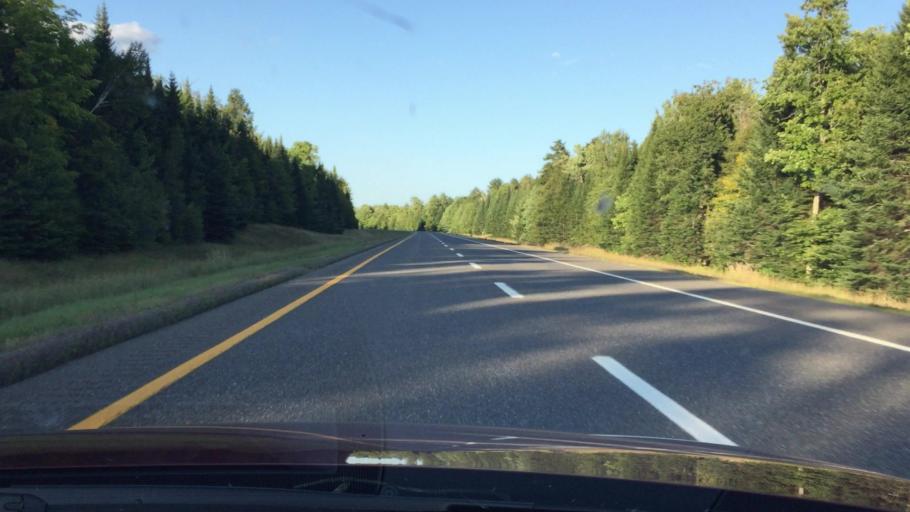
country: US
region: Maine
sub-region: Penobscot County
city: Patten
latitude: 46.0473
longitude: -68.2505
